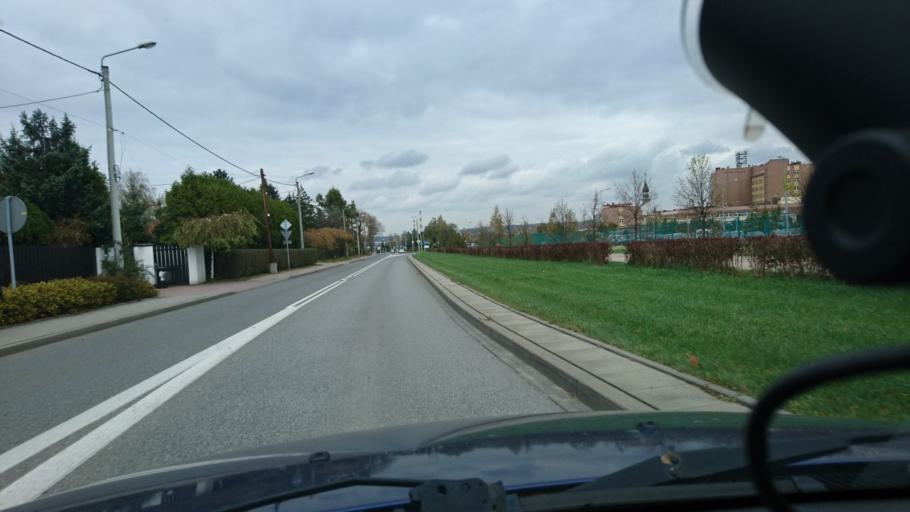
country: PL
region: Silesian Voivodeship
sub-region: Bielsko-Biala
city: Bielsko-Biala
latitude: 49.7908
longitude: 19.0359
